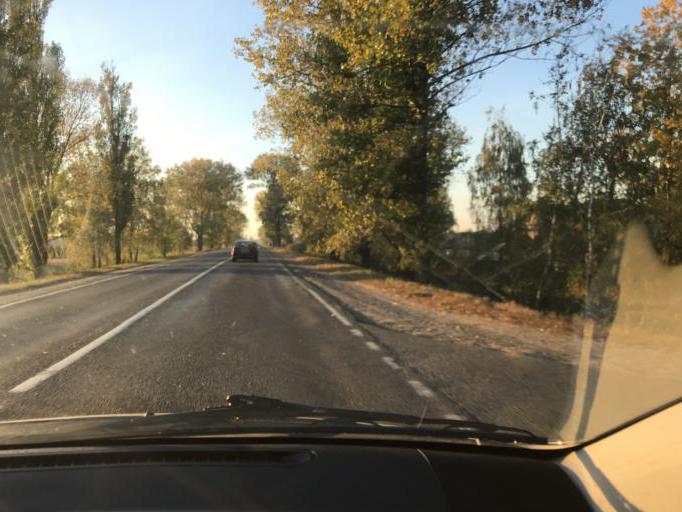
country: BY
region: Brest
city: Pinsk
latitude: 52.0659
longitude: 26.1918
